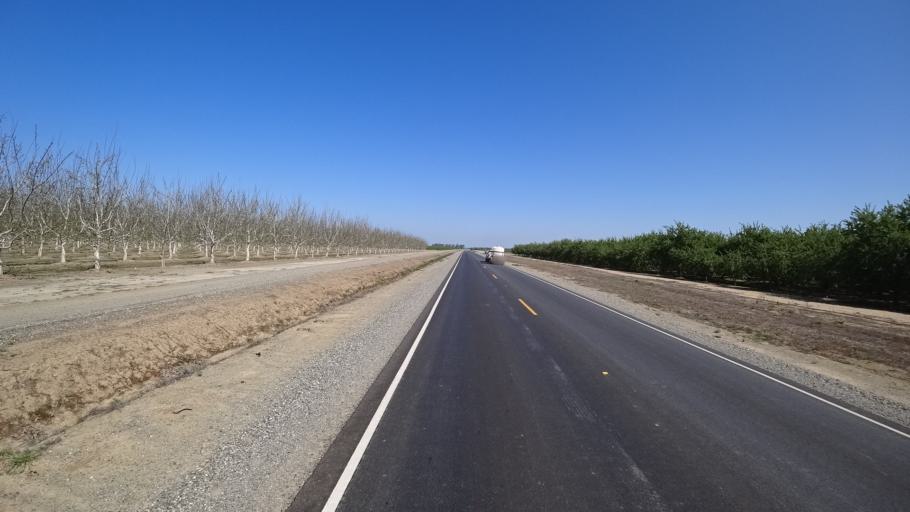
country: US
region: California
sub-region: Glenn County
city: Hamilton City
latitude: 39.6394
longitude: -122.0650
